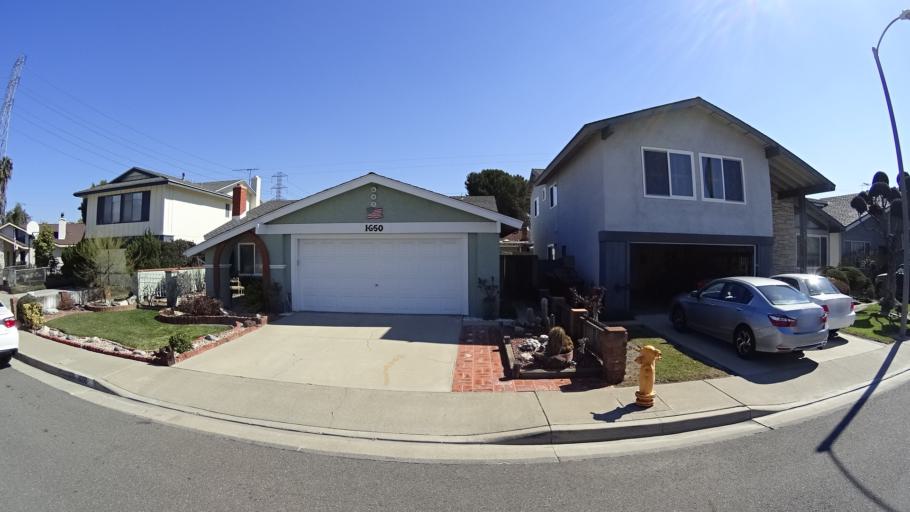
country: US
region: California
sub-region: Orange County
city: Garden Grove
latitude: 33.8062
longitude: -117.9375
